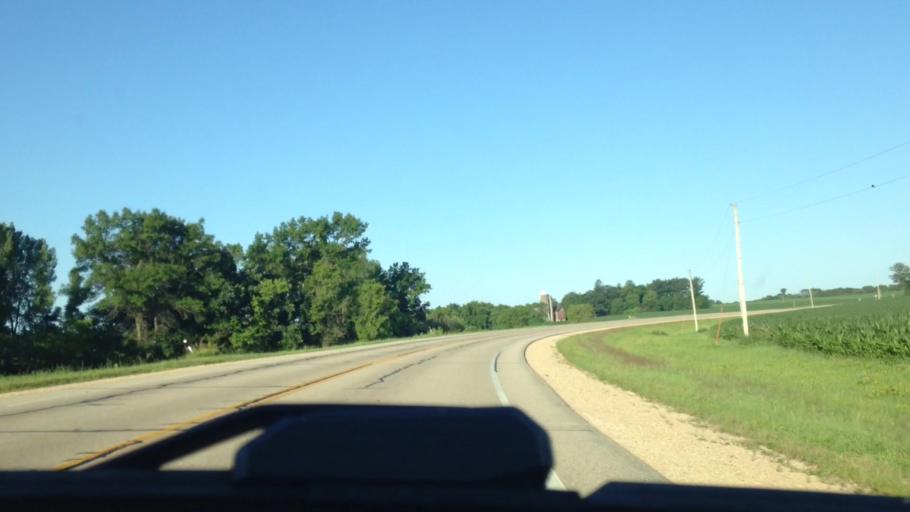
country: US
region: Wisconsin
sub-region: Columbia County
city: Rio
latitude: 43.3336
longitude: -89.2604
